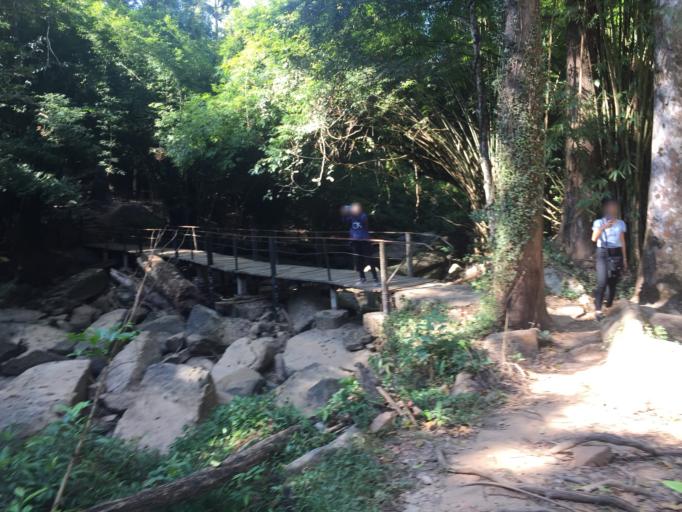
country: TH
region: Phetchabun
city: Khao Kho
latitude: 16.6297
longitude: 100.9395
